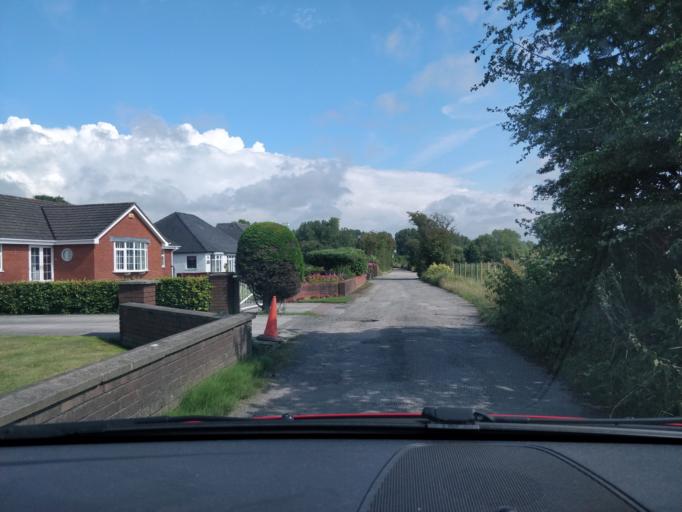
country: GB
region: England
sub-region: Lancashire
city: Banks
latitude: 53.6639
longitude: -2.9530
